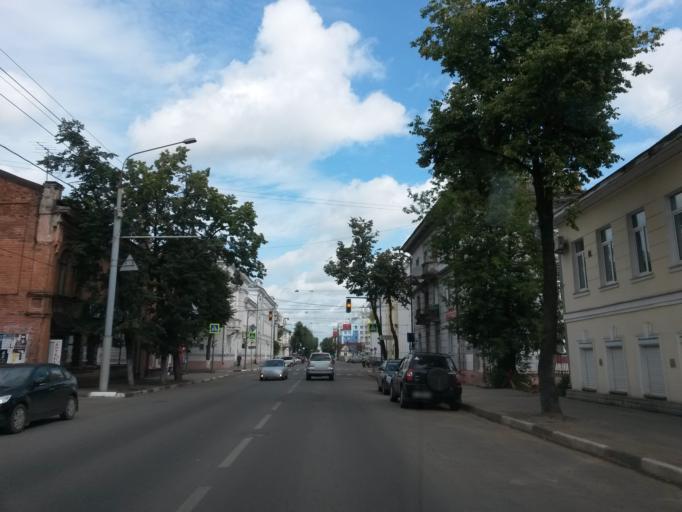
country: RU
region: Jaroslavl
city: Yaroslavl
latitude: 57.6312
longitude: 39.8797
